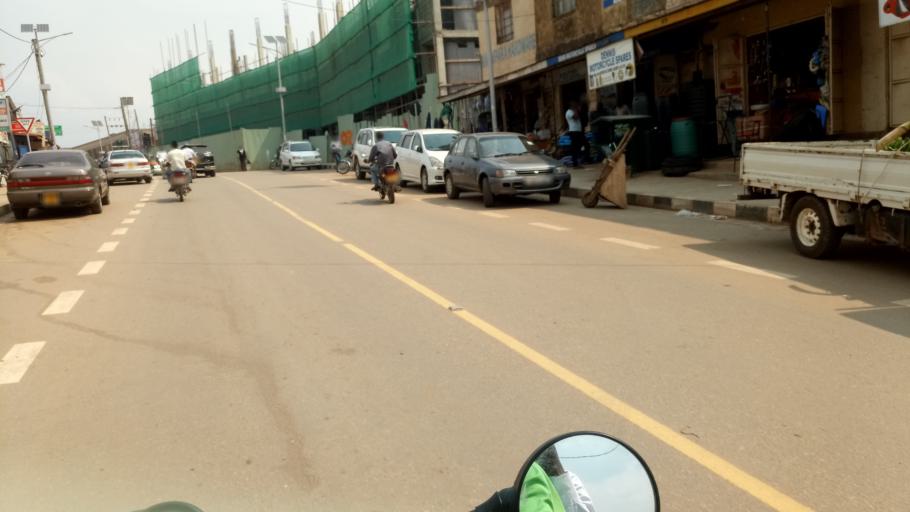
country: UG
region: Western Region
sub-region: Mbarara District
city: Mbarara
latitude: -0.6064
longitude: 30.6634
